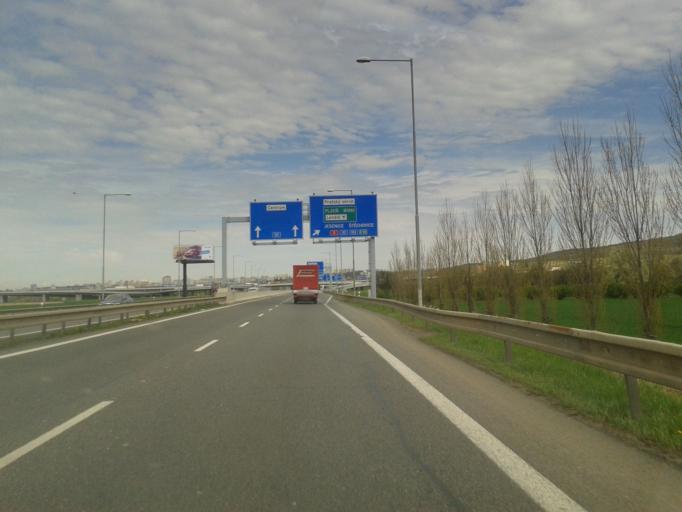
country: CZ
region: Praha
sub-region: Praha 12
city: Modrany
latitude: 49.9799
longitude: 14.3869
